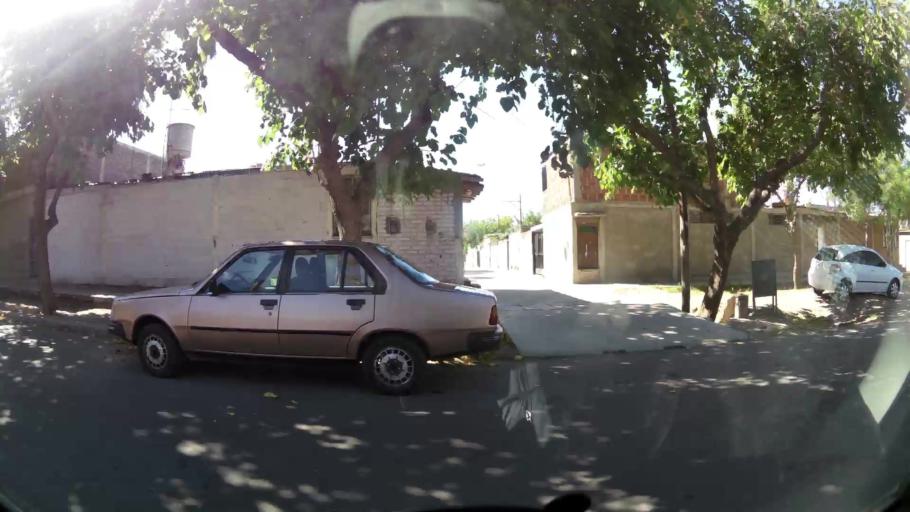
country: AR
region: Mendoza
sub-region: Departamento de Godoy Cruz
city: Godoy Cruz
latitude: -32.9568
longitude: -68.8340
